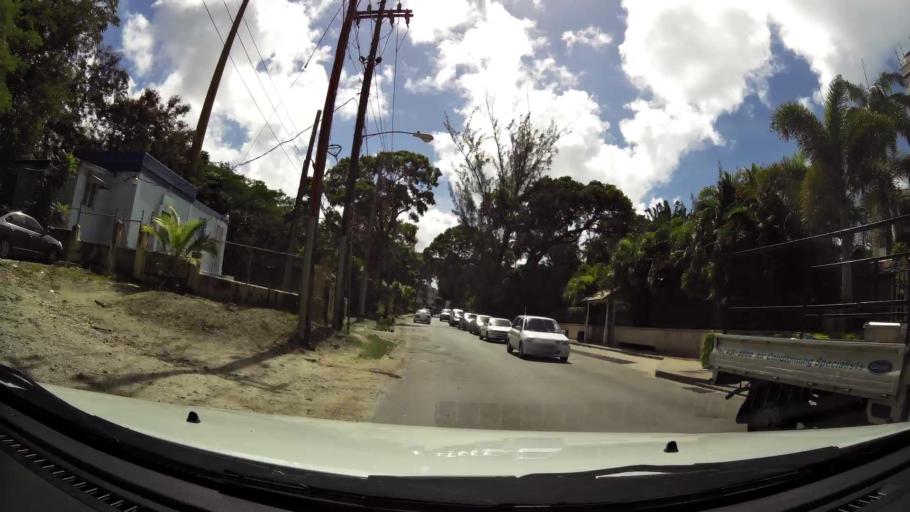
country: BB
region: Saint James
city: Holetown
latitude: 13.1683
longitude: -59.6370
